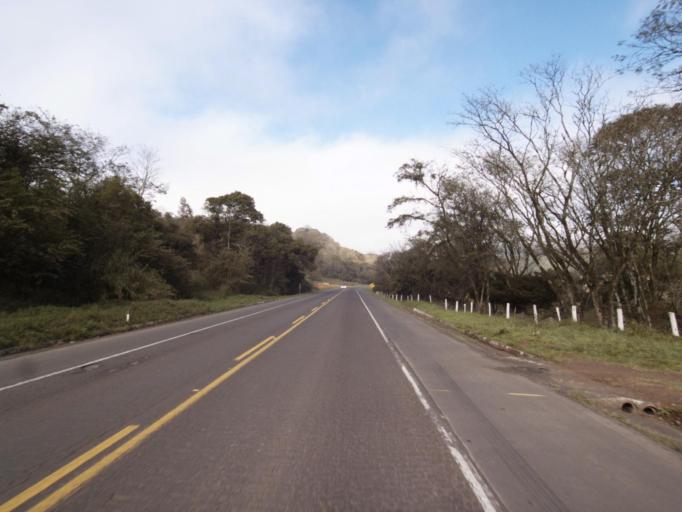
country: BR
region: Rio Grande do Sul
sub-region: Frederico Westphalen
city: Frederico Westphalen
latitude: -27.0143
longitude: -53.2266
